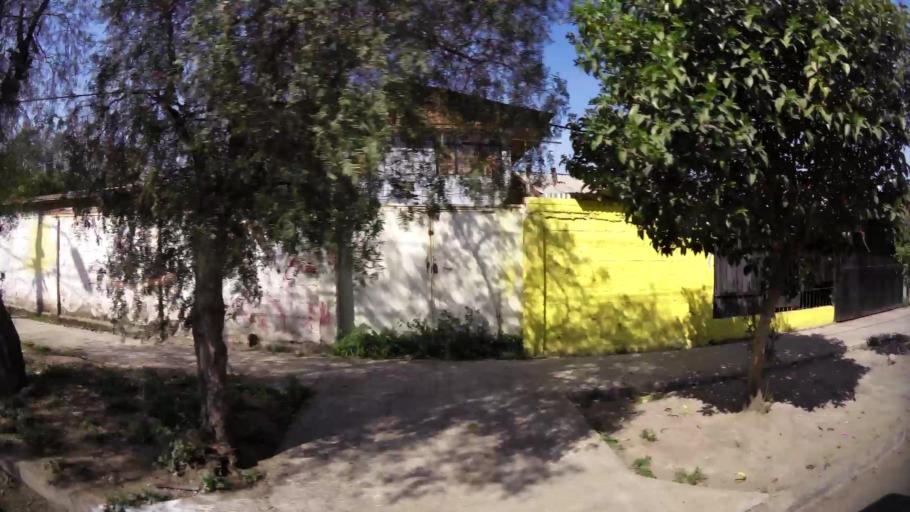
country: CL
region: Santiago Metropolitan
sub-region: Provincia de Santiago
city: La Pintana
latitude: -33.5377
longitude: -70.6327
